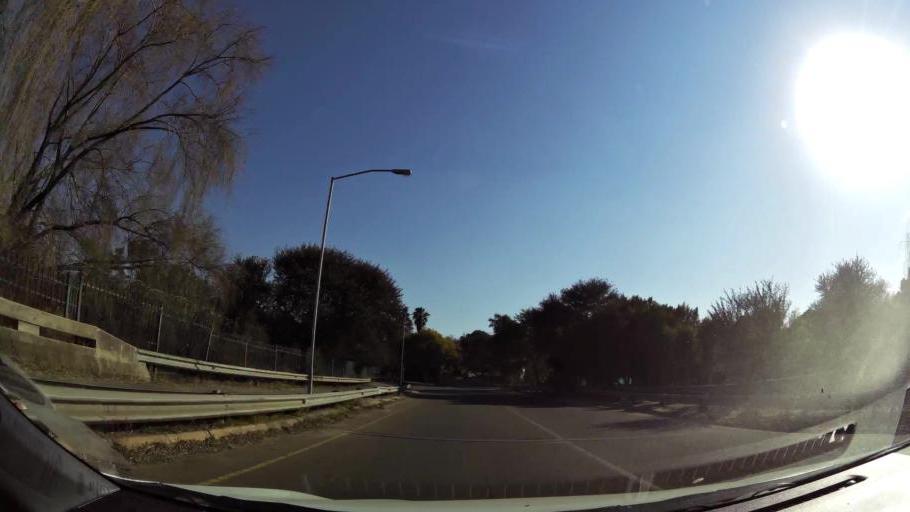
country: ZA
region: Gauteng
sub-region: City of Tshwane Metropolitan Municipality
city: Pretoria
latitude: -25.7957
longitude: 28.2986
